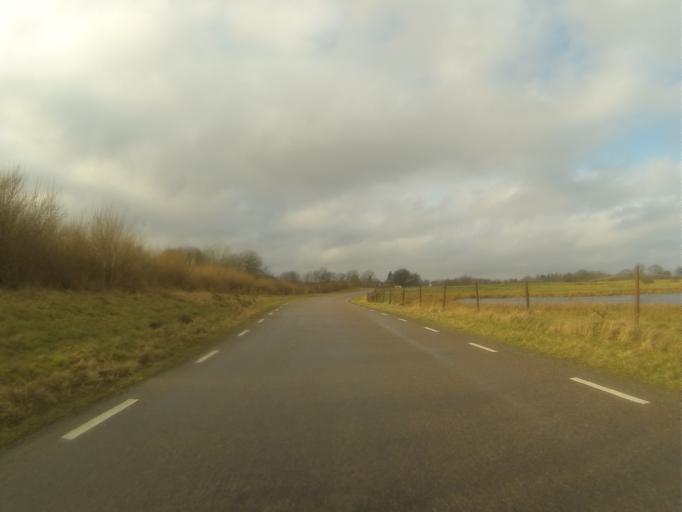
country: SE
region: Skane
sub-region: Svedala Kommun
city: Klagerup
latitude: 55.5671
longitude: 13.3124
